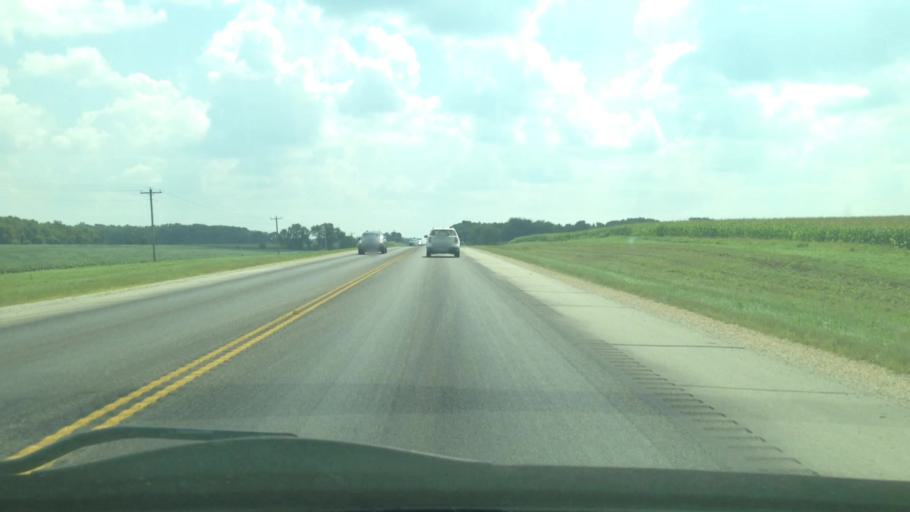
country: US
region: Minnesota
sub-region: Mower County
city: Grand Meadow
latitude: 43.7374
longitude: -92.4795
